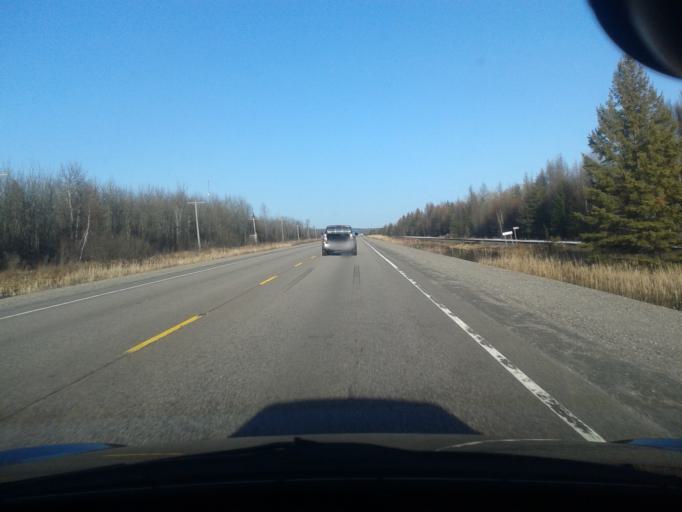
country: CA
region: Ontario
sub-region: Nipissing District
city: North Bay
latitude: 46.3685
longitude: -79.7750
